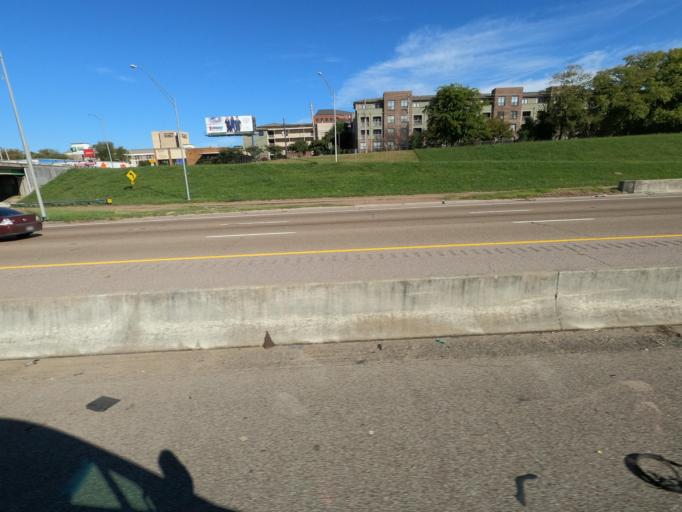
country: US
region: Tennessee
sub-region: Shelby County
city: Memphis
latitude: 35.1368
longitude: -90.0243
